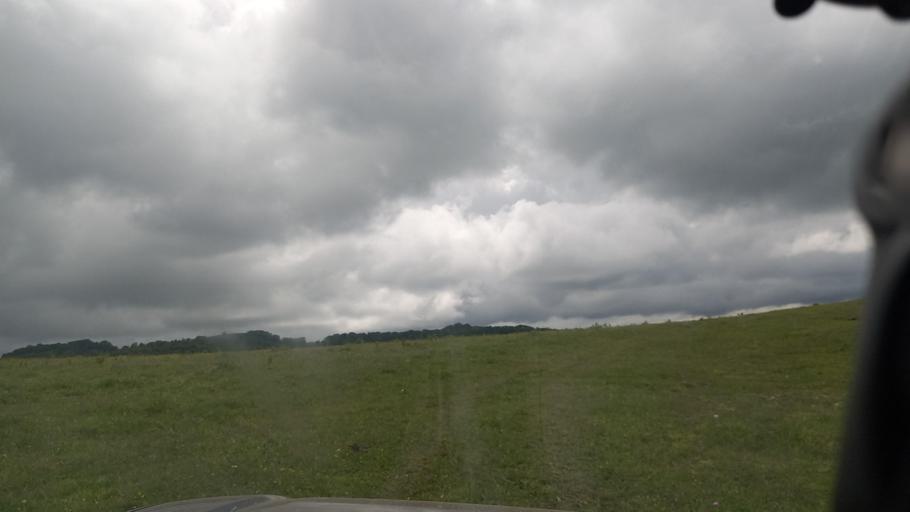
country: RU
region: Karachayevo-Cherkesiya
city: Pregradnaya
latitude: 43.9905
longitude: 41.2831
